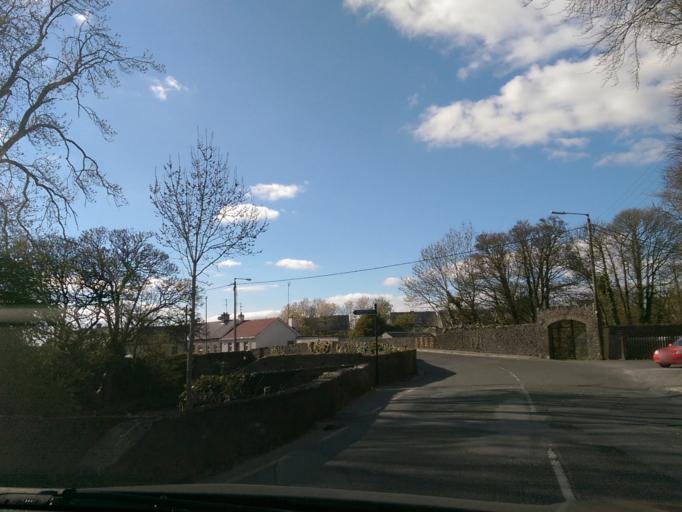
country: IE
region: Leinster
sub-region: Uibh Fhaili
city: Birr
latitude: 53.0950
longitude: -7.9003
